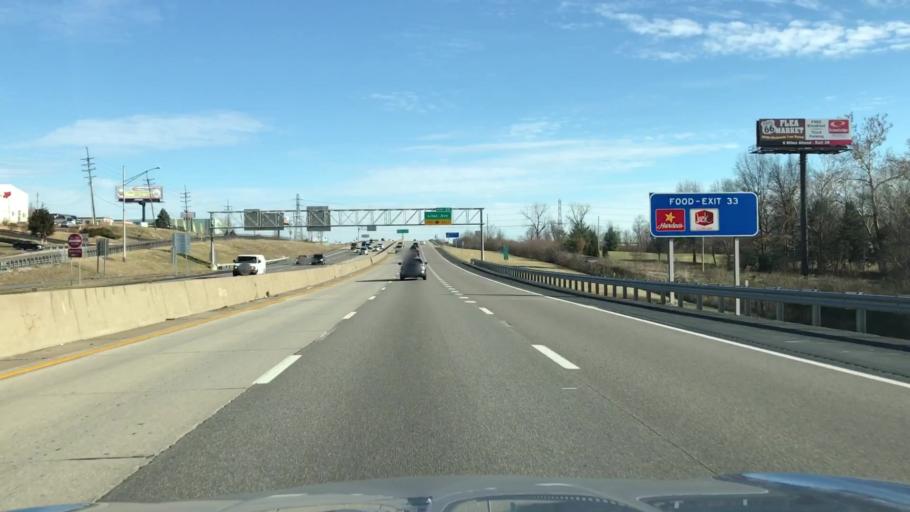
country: US
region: Missouri
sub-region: Saint Louis County
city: Spanish Lake
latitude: 38.7689
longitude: -90.2156
